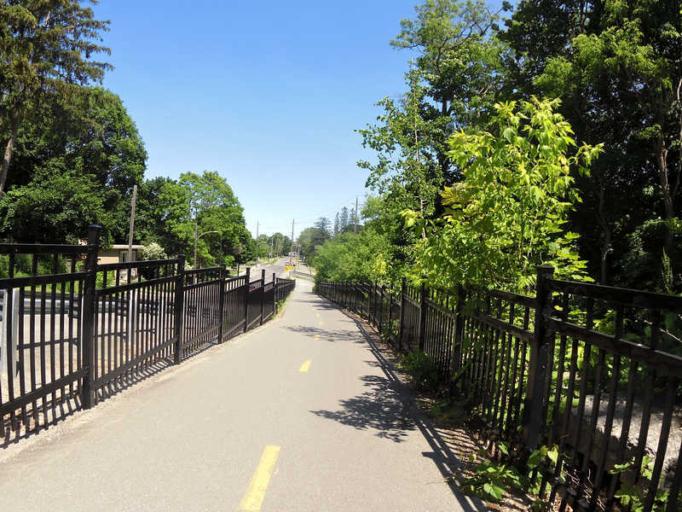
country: CA
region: Ontario
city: Peterborough
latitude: 44.3006
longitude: -78.3125
